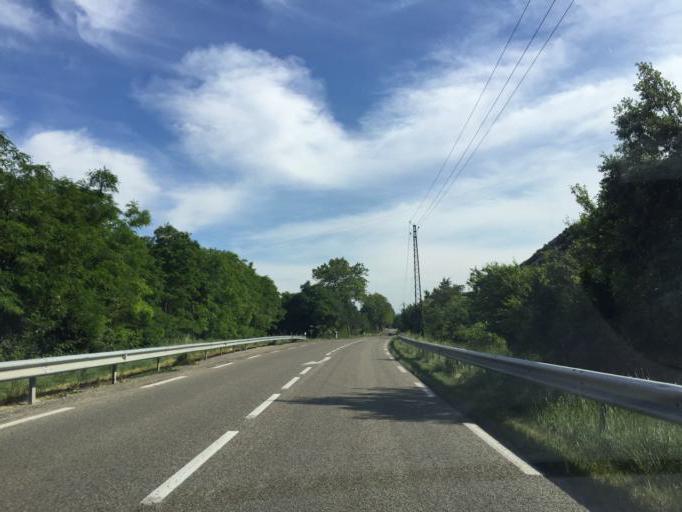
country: FR
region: Rhone-Alpes
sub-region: Departement de l'Ardeche
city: Cruas
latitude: 44.6786
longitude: 4.7714
